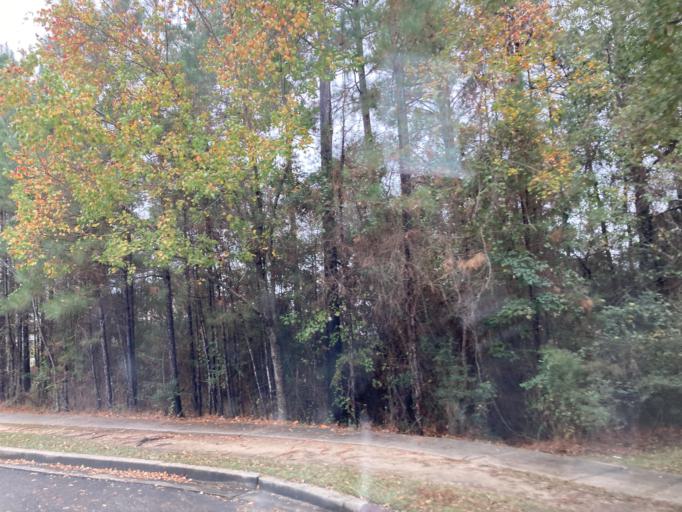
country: US
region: Mississippi
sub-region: Lamar County
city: West Hattiesburg
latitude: 31.2829
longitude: -89.4729
